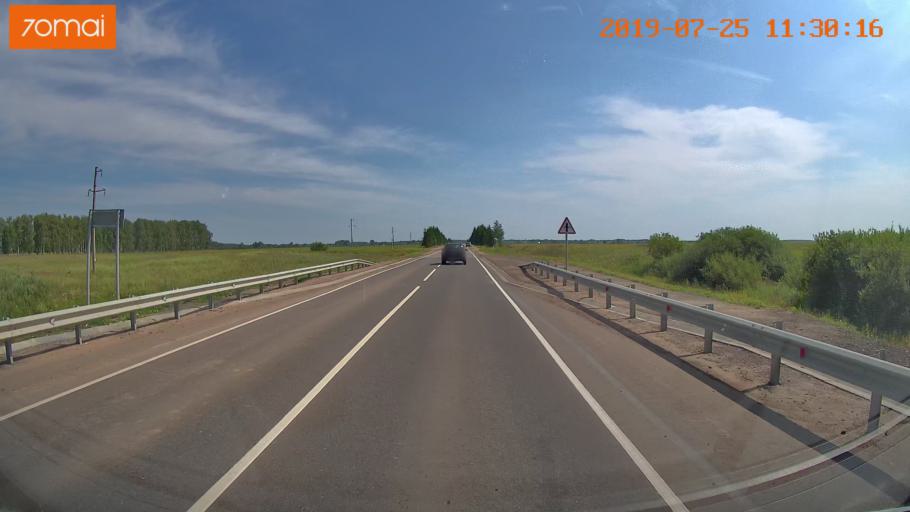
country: RU
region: Ivanovo
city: Privolzhsk
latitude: 57.3867
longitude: 41.3199
